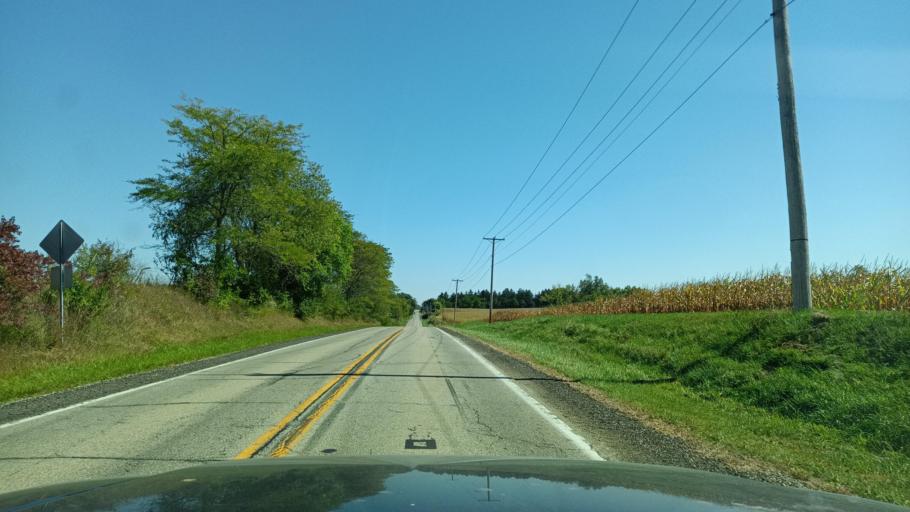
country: US
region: Illinois
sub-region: McLean County
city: Danvers
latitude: 40.6168
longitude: -89.2315
